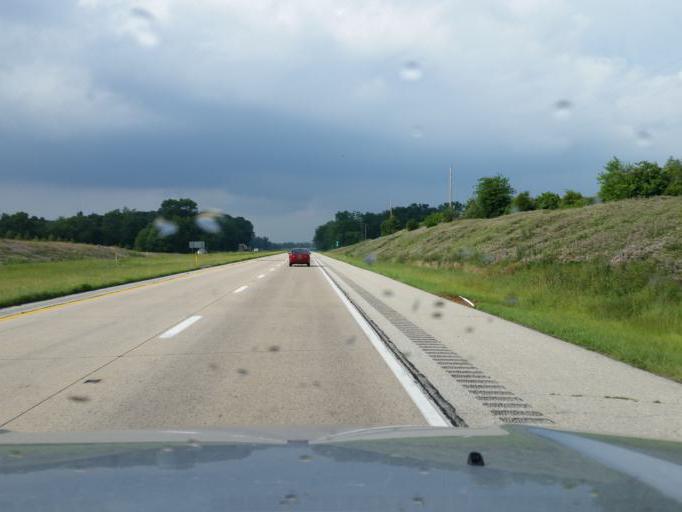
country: US
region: Pennsylvania
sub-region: Adams County
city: Gettysburg
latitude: 39.8782
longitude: -77.1888
